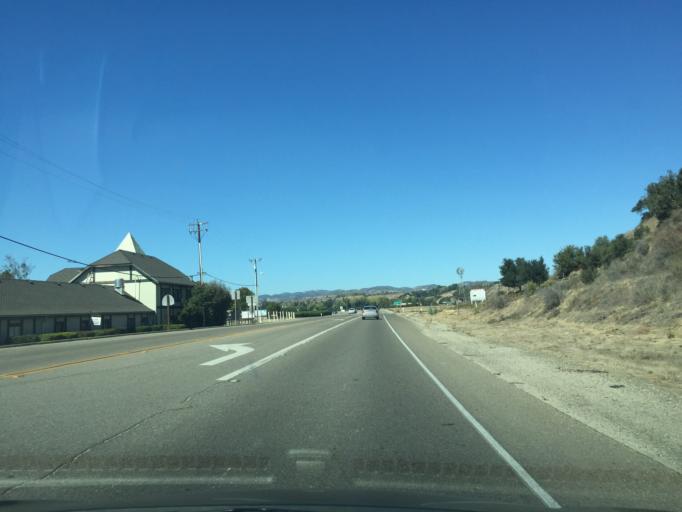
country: US
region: California
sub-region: Santa Barbara County
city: Solvang
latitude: 34.5950
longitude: -120.1536
